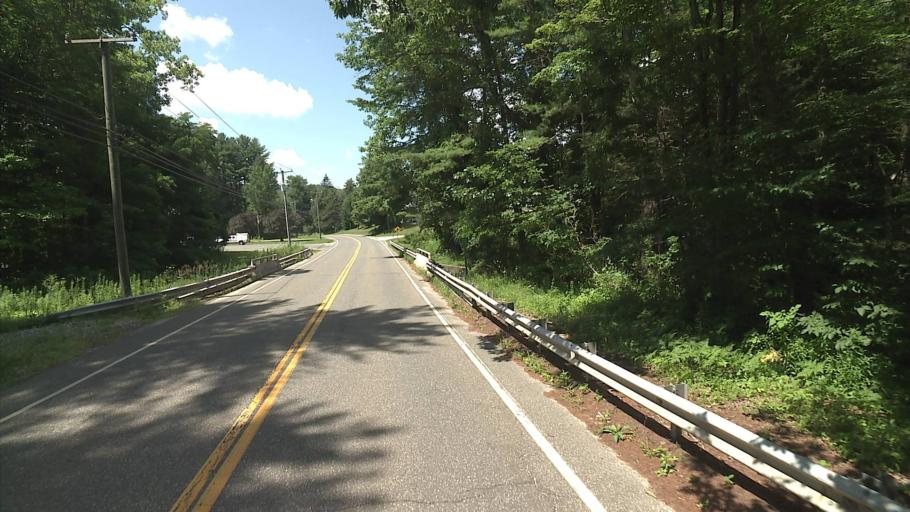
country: US
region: Connecticut
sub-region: Litchfield County
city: Canaan
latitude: 41.8752
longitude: -73.3400
